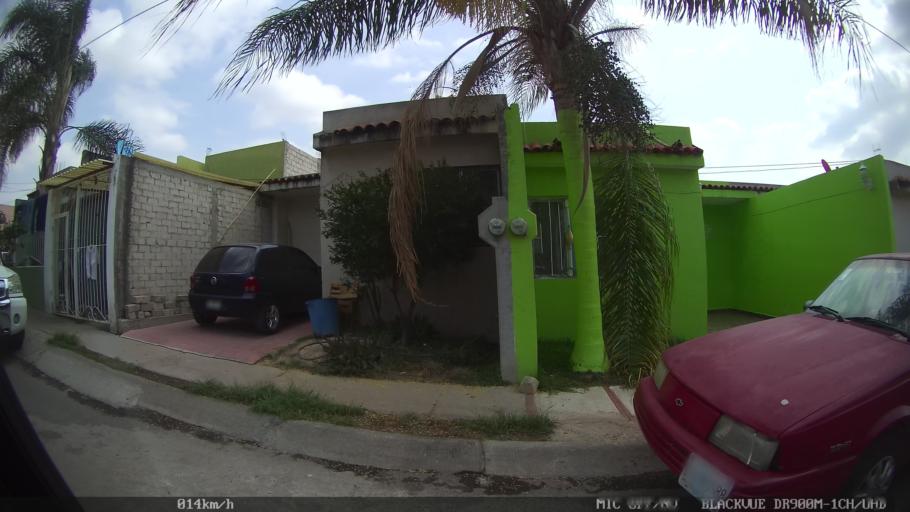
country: MX
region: Jalisco
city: Coyula
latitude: 20.6392
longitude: -103.2160
